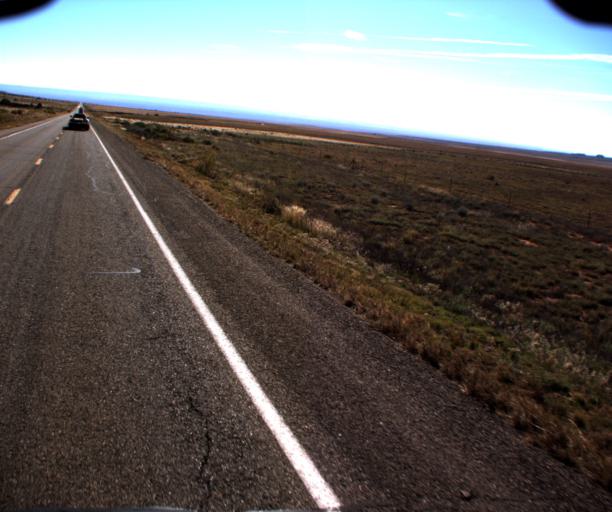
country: US
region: Arizona
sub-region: Mohave County
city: Colorado City
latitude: 36.8781
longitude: -112.8837
